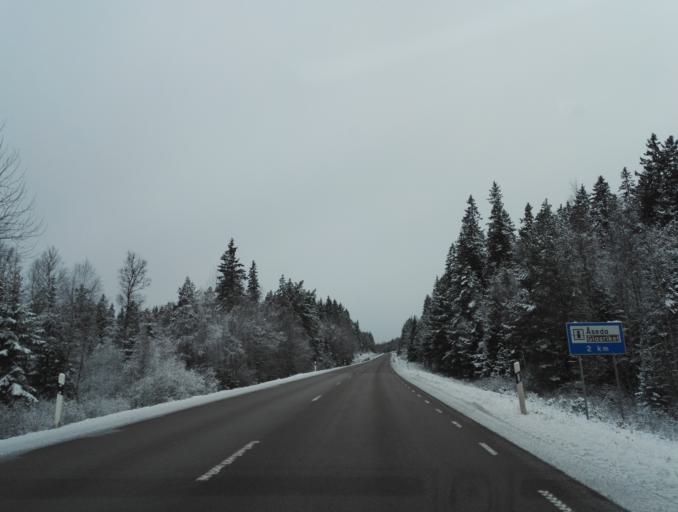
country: SE
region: Kronoberg
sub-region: Uppvidinge Kommun
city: Aseda
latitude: 57.1626
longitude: 15.4096
